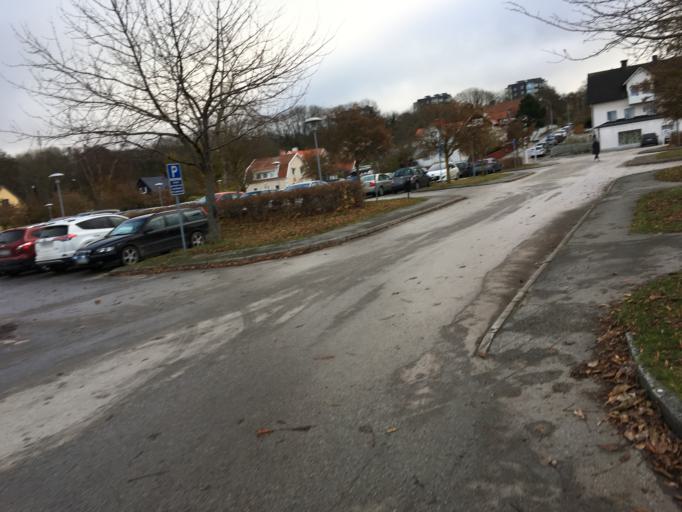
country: SE
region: Gotland
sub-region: Gotland
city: Visby
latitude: 57.6498
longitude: 18.3021
